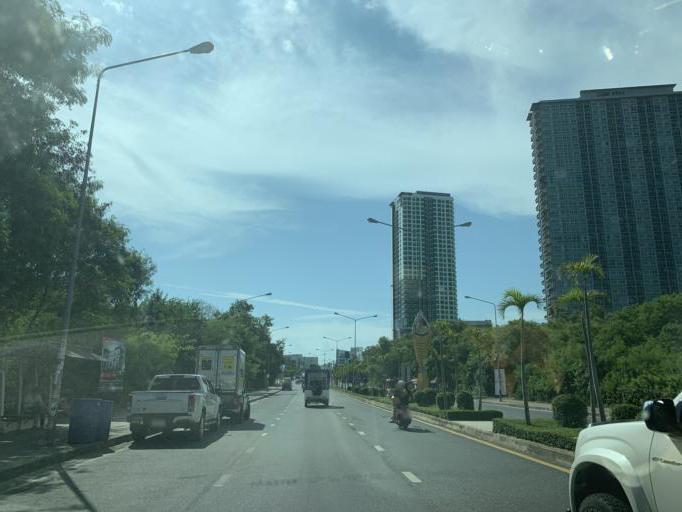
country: TH
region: Chon Buri
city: Phatthaya
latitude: 12.8909
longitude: 100.8790
